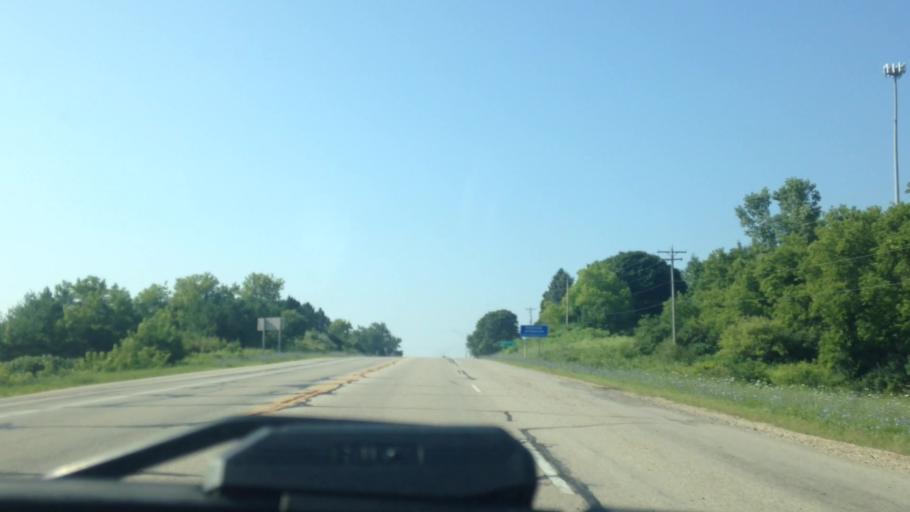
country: US
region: Wisconsin
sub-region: Waukesha County
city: Merton
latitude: 43.1657
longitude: -88.2626
